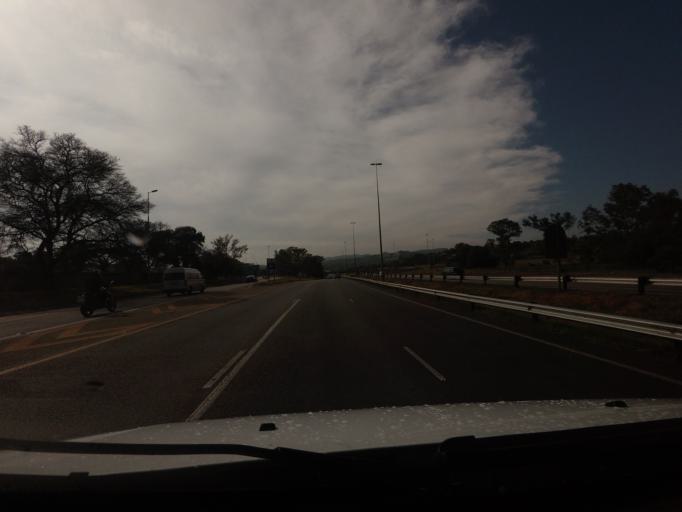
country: ZA
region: Gauteng
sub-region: City of Tshwane Metropolitan Municipality
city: Pretoria
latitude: -25.7438
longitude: 28.2902
